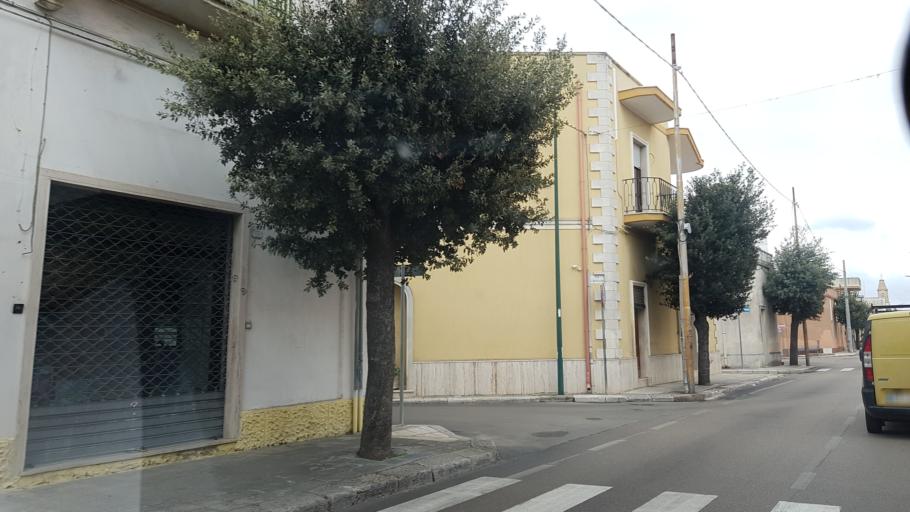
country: IT
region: Apulia
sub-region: Provincia di Lecce
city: Guagnano
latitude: 40.4008
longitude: 17.9477
